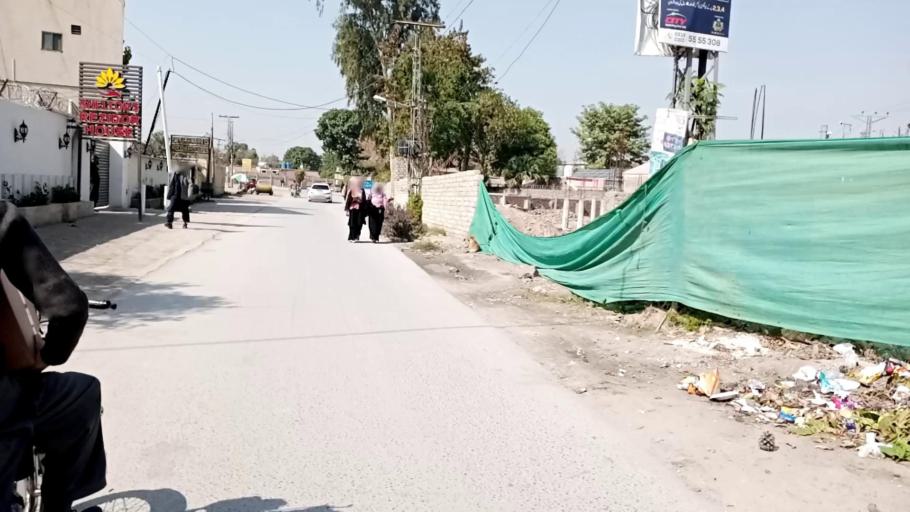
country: PK
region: Khyber Pakhtunkhwa
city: Peshawar
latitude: 33.9974
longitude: 71.5019
